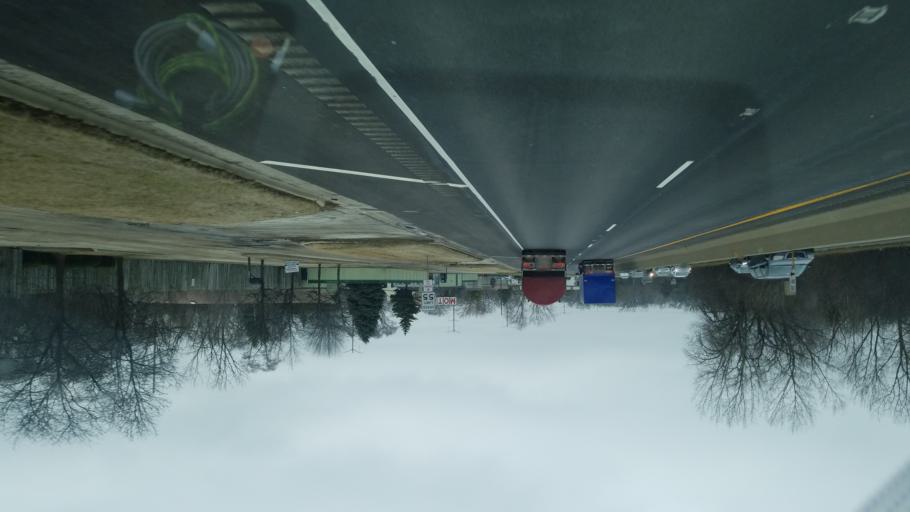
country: US
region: Illinois
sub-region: Lake County
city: Knollwood
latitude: 42.2823
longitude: -87.8705
